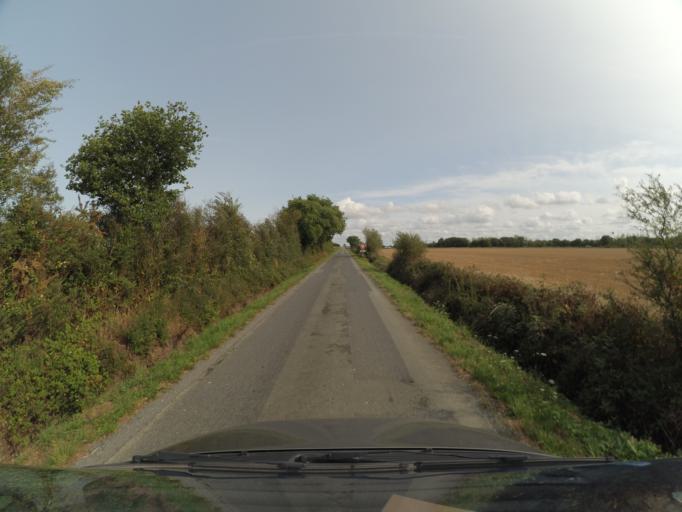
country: FR
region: Pays de la Loire
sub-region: Departement de la Vendee
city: La Bruffiere
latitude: 46.9919
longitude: -1.1893
